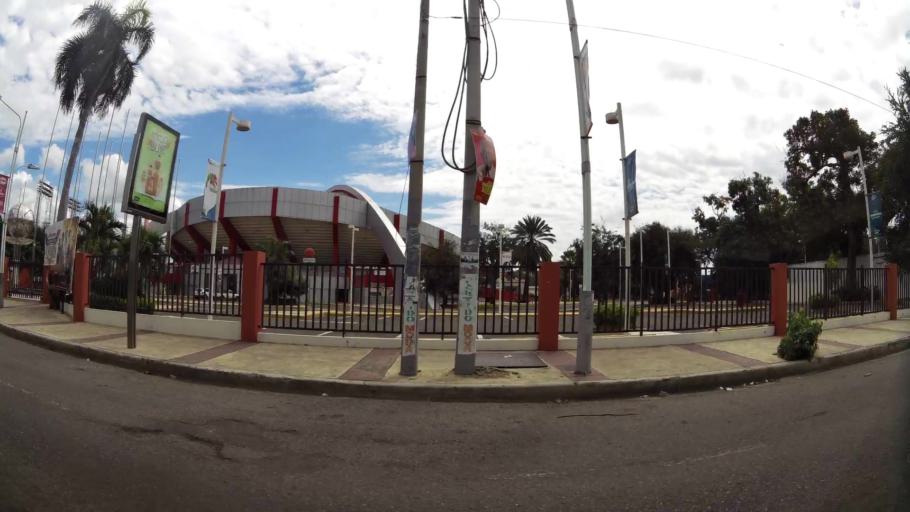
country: DO
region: Santiago
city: Santiago de los Caballeros
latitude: 19.4654
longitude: -70.7106
